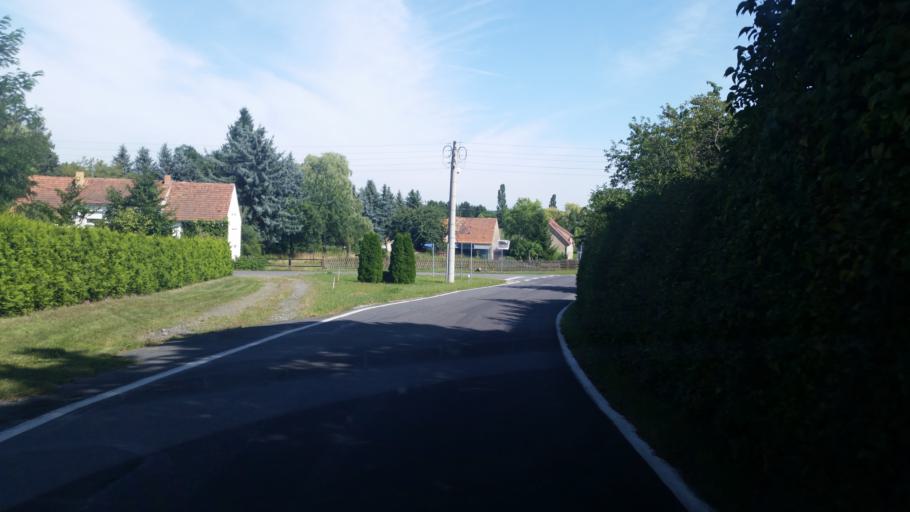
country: DE
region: Saxony
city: Schwepnitz
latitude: 51.3354
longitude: 14.0076
